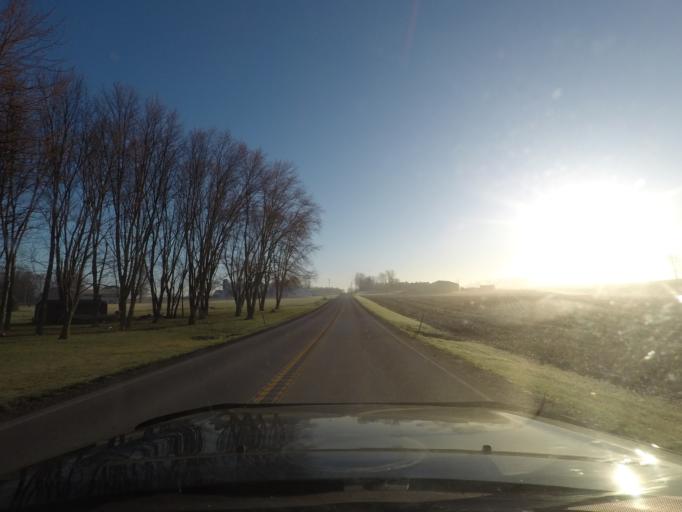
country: US
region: Indiana
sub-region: Elkhart County
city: Wakarusa
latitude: 41.5346
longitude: -85.9433
